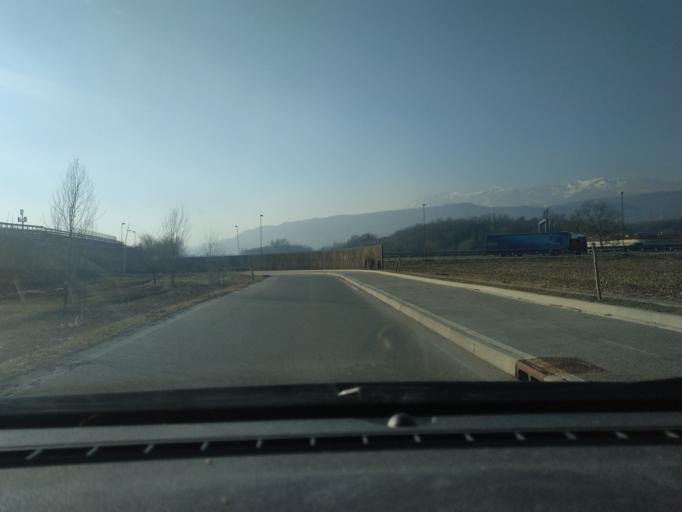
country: IT
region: Piedmont
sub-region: Provincia di Torino
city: Pavone Canavese
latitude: 45.4476
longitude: 7.8517
